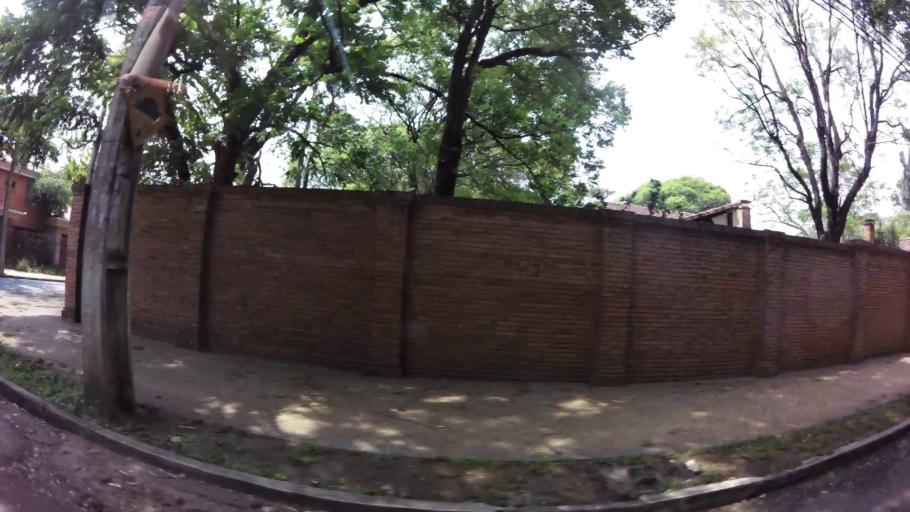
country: PY
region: Asuncion
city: Asuncion
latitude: -25.2873
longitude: -57.5812
